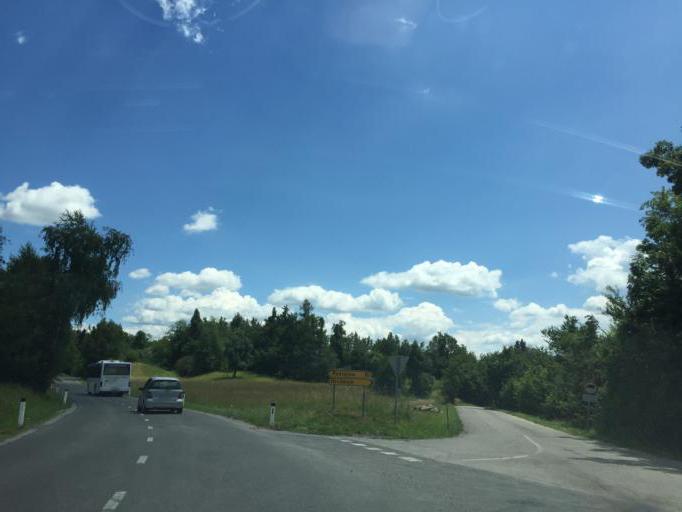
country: SI
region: Postojna
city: Postojna
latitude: 45.8099
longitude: 14.1467
